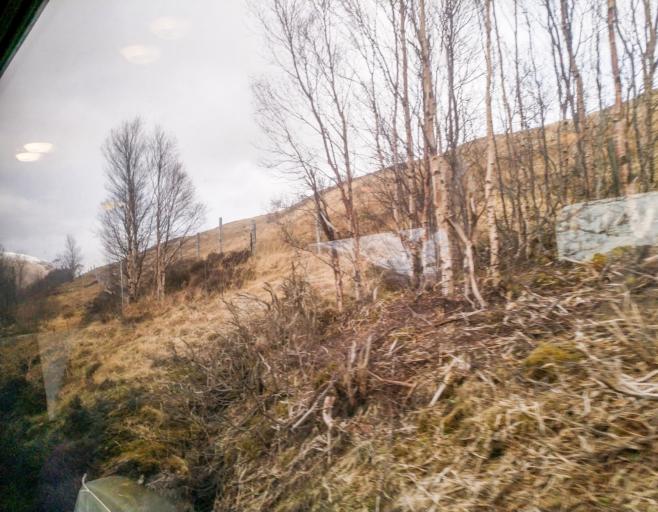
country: GB
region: Scotland
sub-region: Highland
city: Spean Bridge
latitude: 56.7795
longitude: -4.7328
